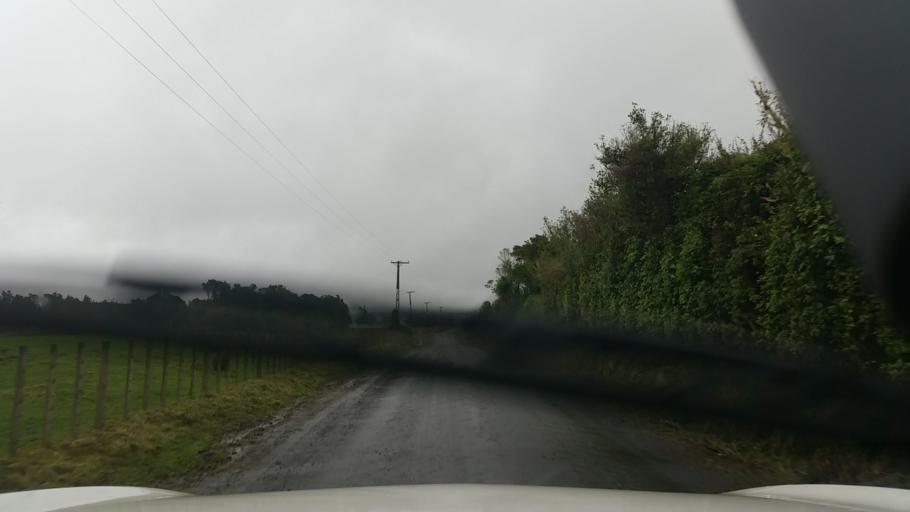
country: NZ
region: Taranaki
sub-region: South Taranaki District
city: Eltham
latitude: -39.2721
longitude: 174.1980
